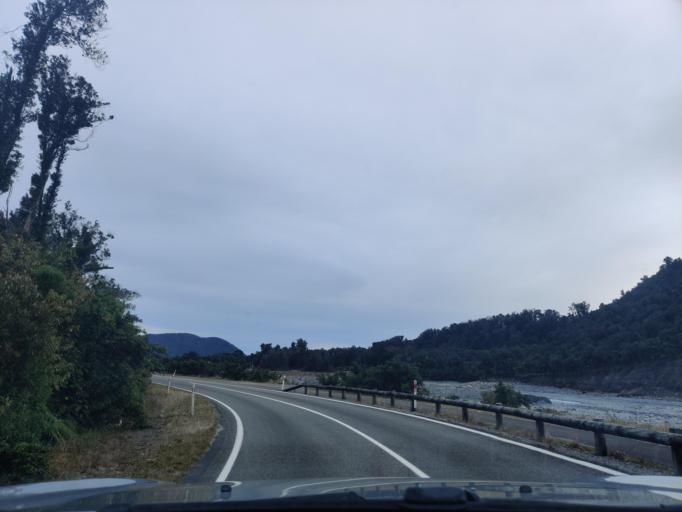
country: NZ
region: West Coast
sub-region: Westland District
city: Hokitika
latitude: -43.3978
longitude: 170.1817
